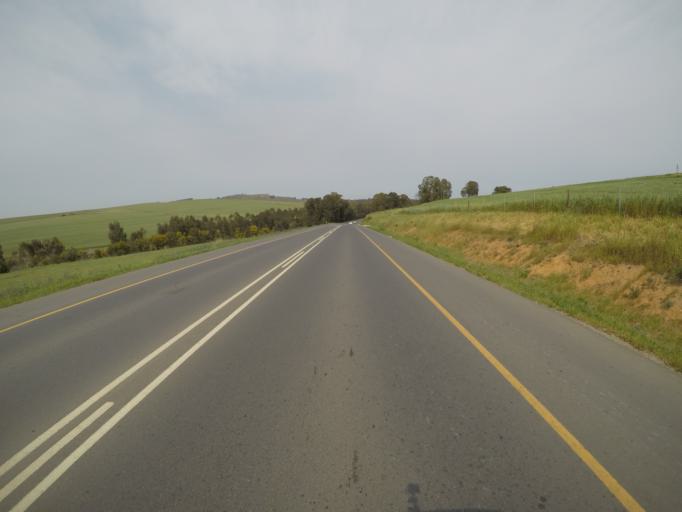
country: ZA
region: Western Cape
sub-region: West Coast District Municipality
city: Malmesbury
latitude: -33.4558
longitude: 18.7477
